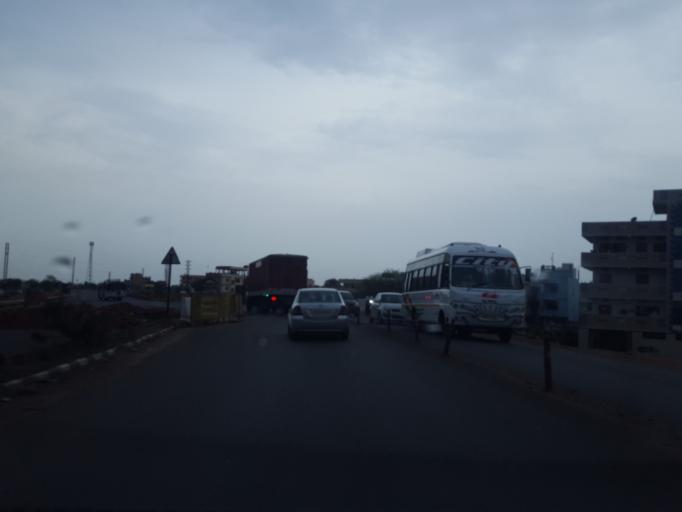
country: IN
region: Telangana
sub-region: Mahbubnagar
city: Farrukhnagar
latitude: 17.1497
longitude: 78.2903
